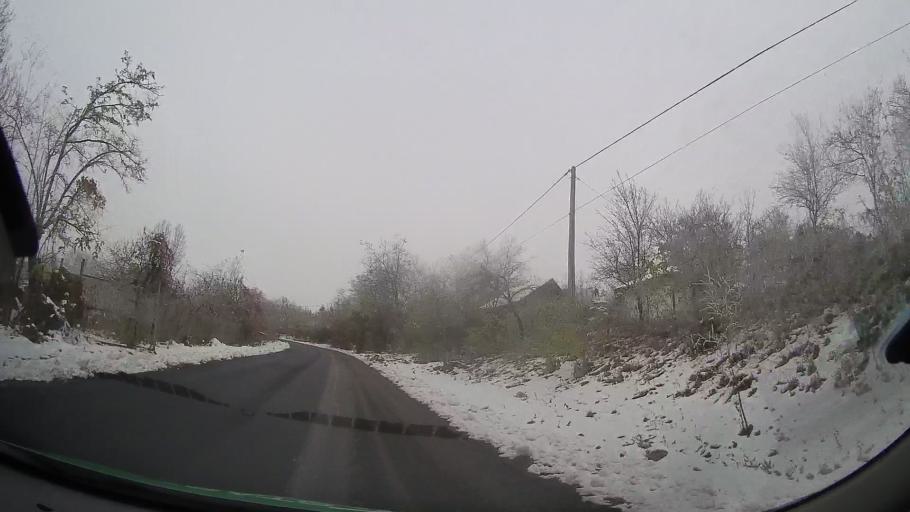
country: RO
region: Vaslui
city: Coroiesti
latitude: 46.2114
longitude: 27.4418
